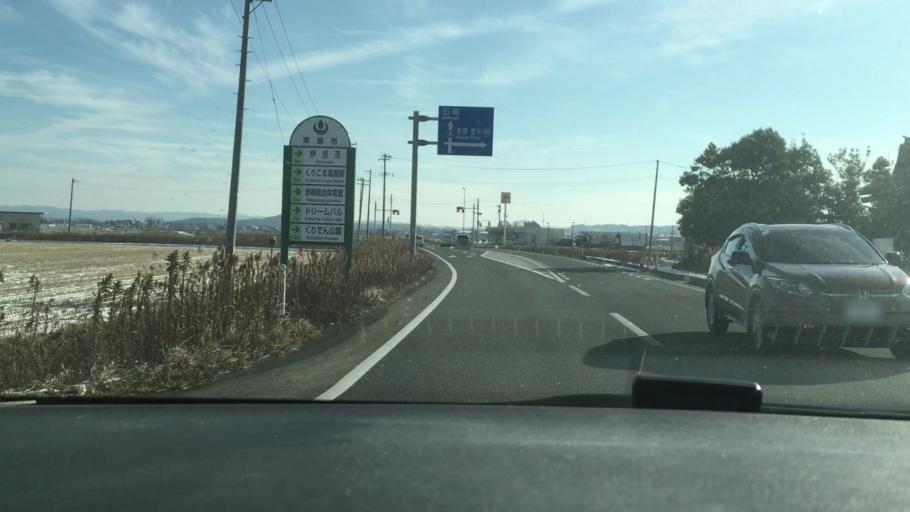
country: JP
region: Iwate
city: Ichinoseki
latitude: 38.7775
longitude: 141.1307
